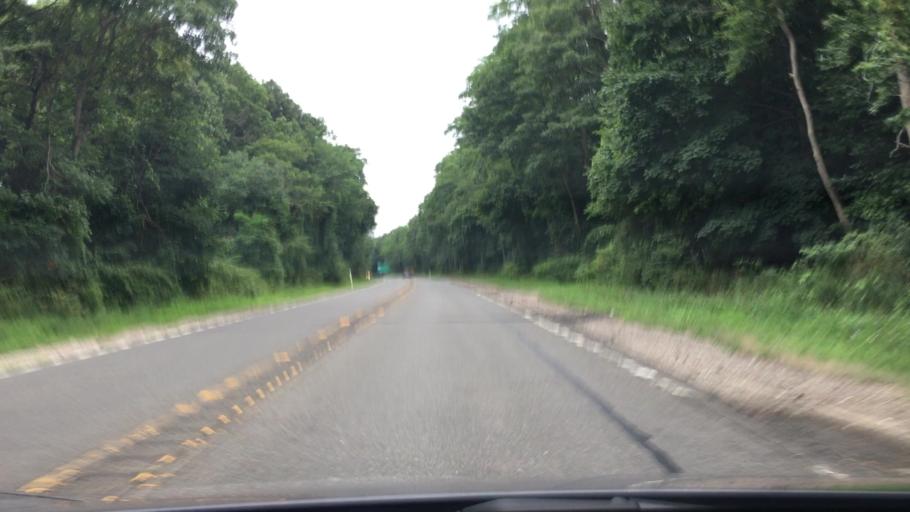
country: US
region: New York
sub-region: Nassau County
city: Bethpage
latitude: 40.7313
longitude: -73.4698
